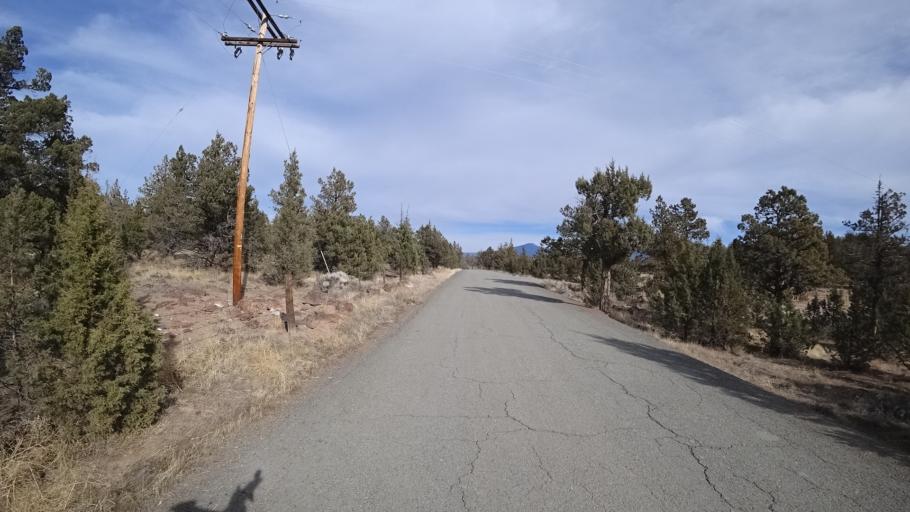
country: US
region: California
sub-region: Siskiyou County
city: Montague
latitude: 41.5870
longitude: -122.4430
